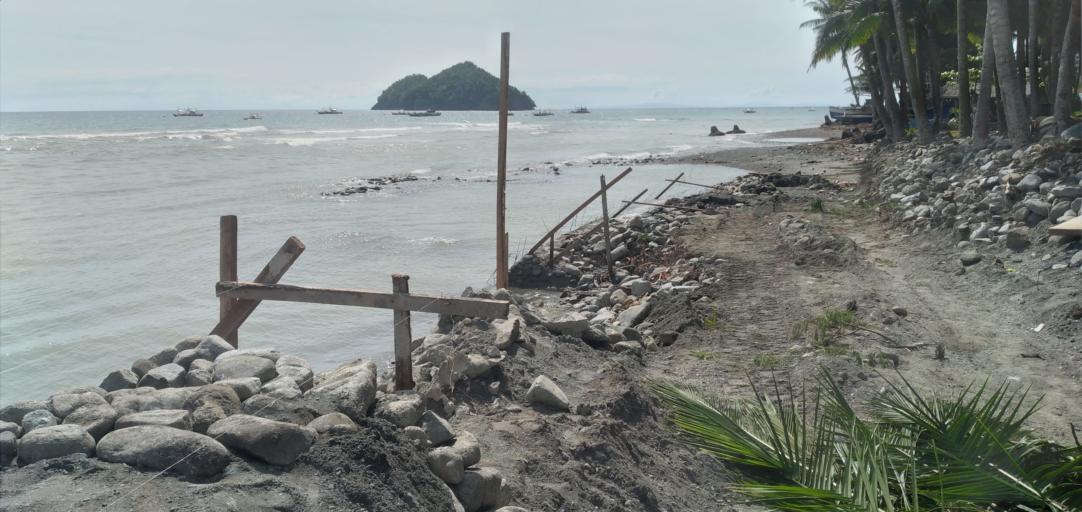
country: PH
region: Davao
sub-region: Province of Davao Oriental
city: Tibanbang
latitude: 6.6199
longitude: 126.0793
